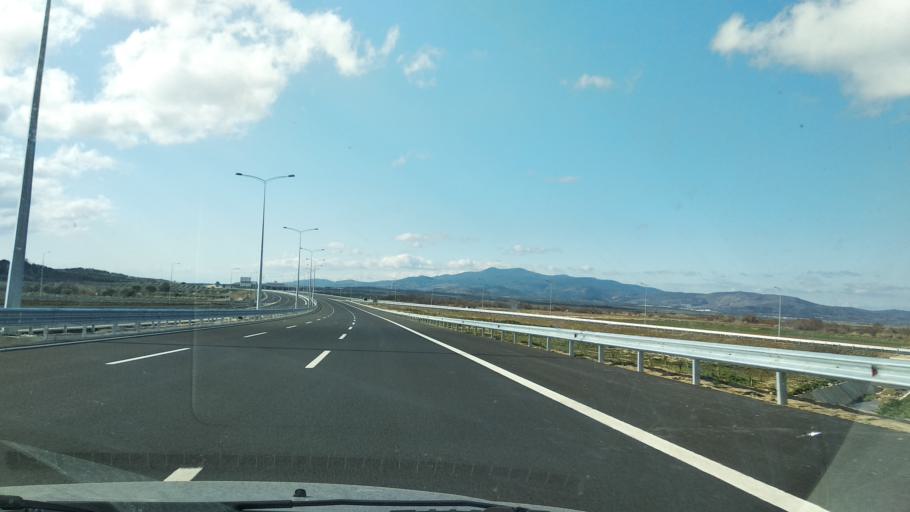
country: TR
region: Izmir
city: Zeytindag
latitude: 38.9729
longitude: 27.0427
